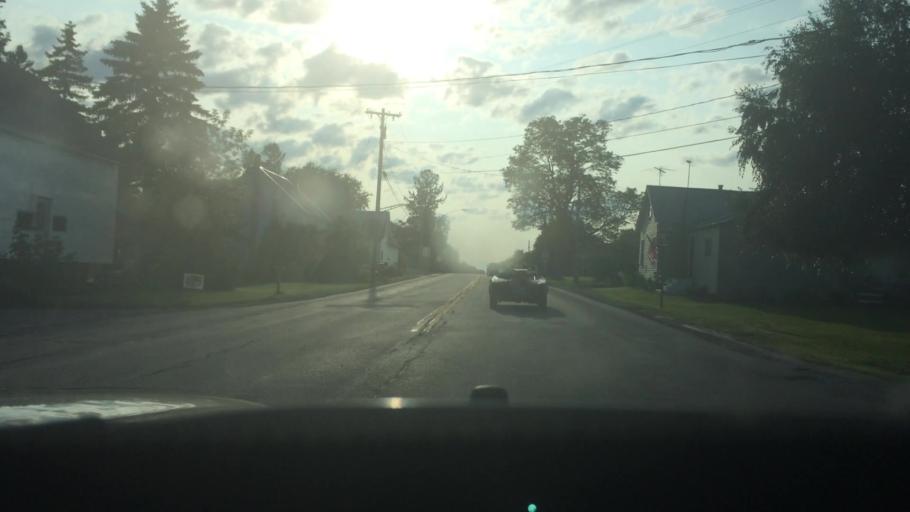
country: US
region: New York
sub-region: St. Lawrence County
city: Ogdensburg
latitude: 44.6655
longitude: -75.3575
